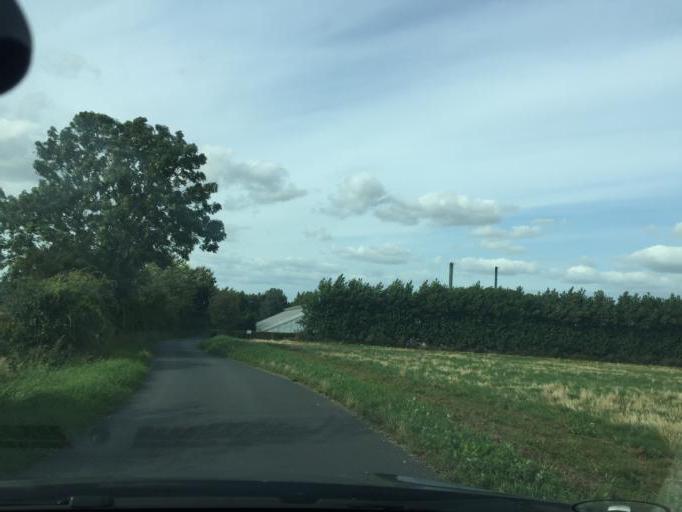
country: DK
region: South Denmark
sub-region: Faaborg-Midtfyn Kommune
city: Arslev
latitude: 55.3442
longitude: 10.5133
